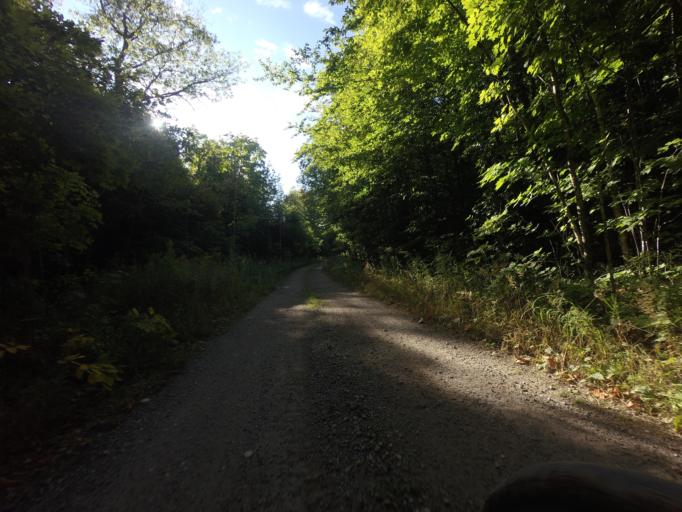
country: CA
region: Ontario
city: Arnprior
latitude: 45.1979
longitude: -76.5244
